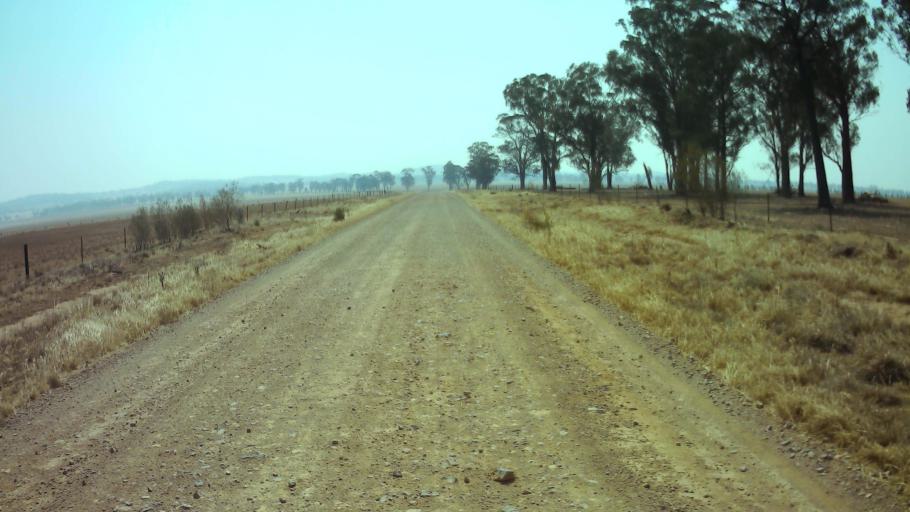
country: AU
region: New South Wales
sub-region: Weddin
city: Grenfell
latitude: -33.6372
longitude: 148.2285
